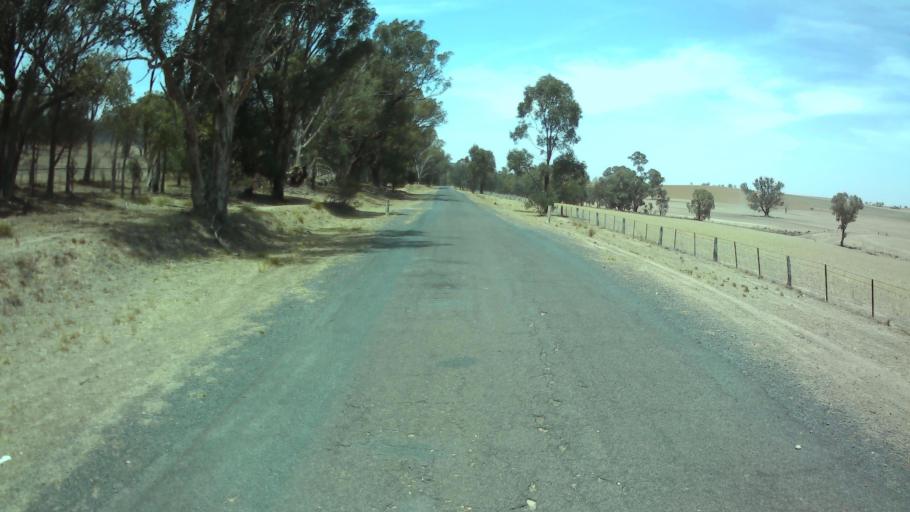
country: AU
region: New South Wales
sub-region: Weddin
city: Grenfell
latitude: -34.0232
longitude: 148.4322
